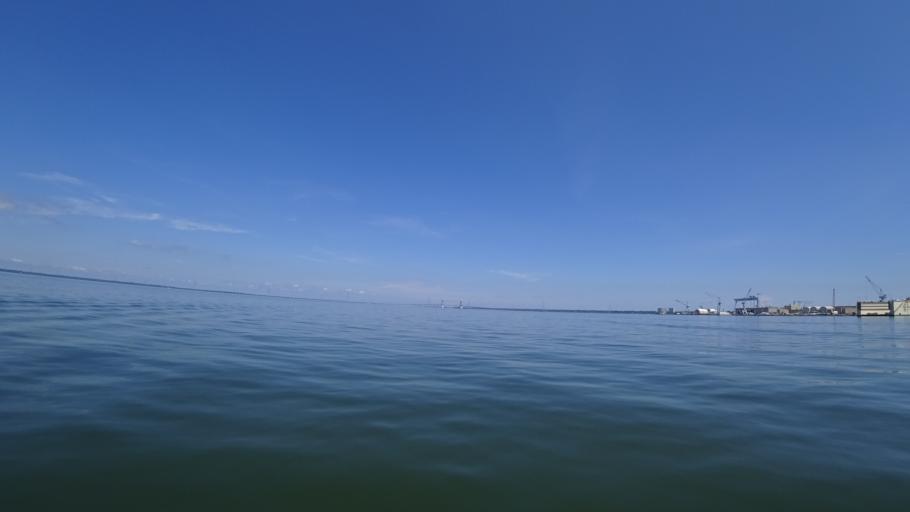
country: US
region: Virginia
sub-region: City of Newport News
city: Newport News
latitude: 36.9836
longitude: -76.4503
